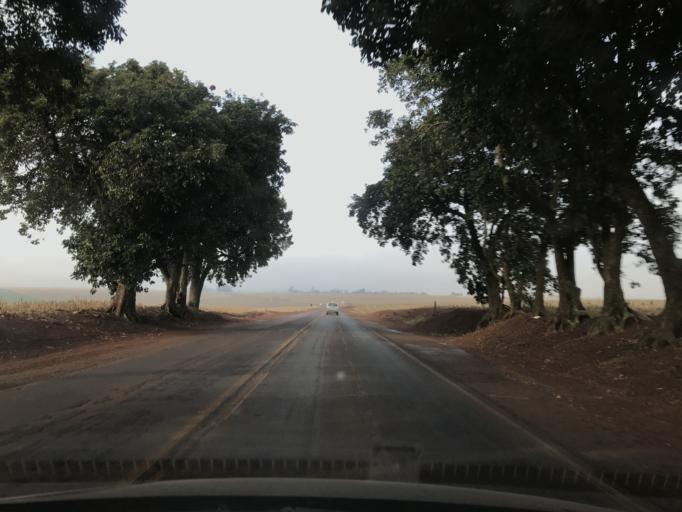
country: BR
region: Parana
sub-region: Toledo
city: Toledo
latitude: -24.5818
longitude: -53.7224
